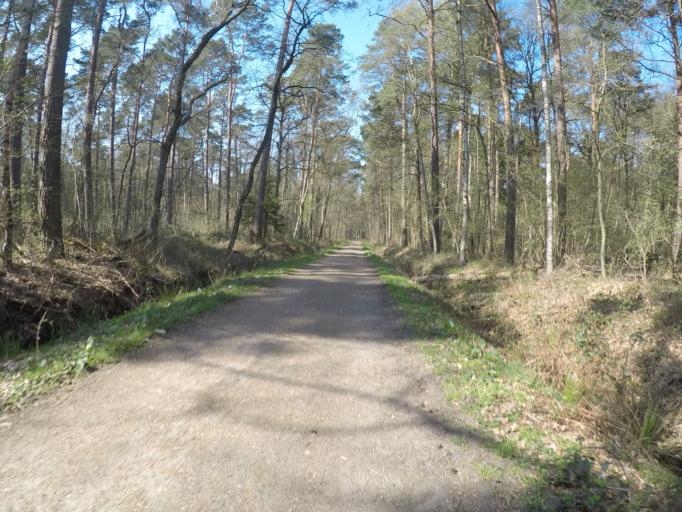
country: DE
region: Schleswig-Holstein
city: Rellingen
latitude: 53.6098
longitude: 9.7893
